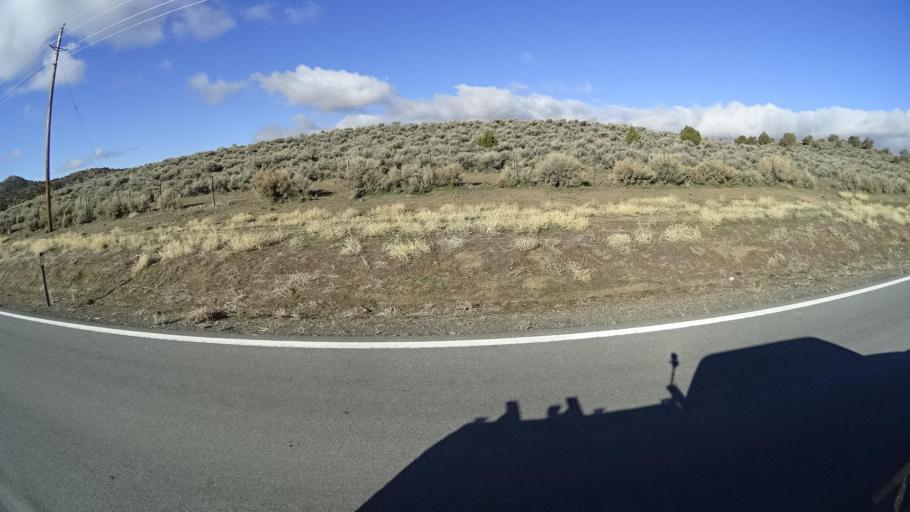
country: US
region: Nevada
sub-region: Washoe County
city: Cold Springs
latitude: 39.7452
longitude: -119.8858
